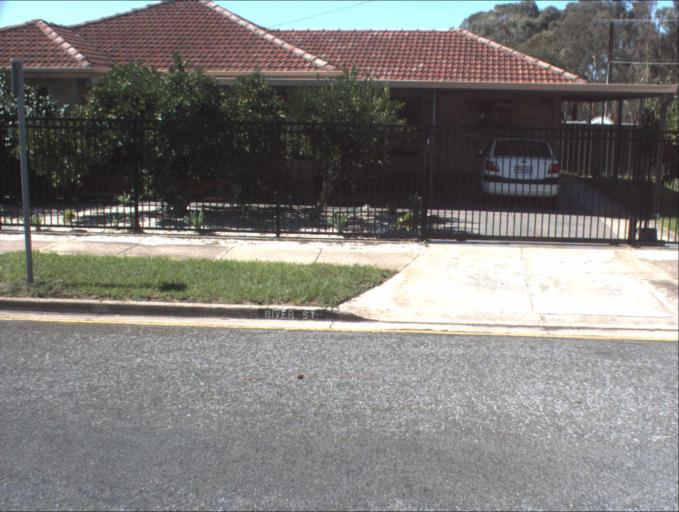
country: AU
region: South Australia
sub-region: Port Adelaide Enfield
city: Klemzig
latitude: -34.8846
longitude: 138.6418
